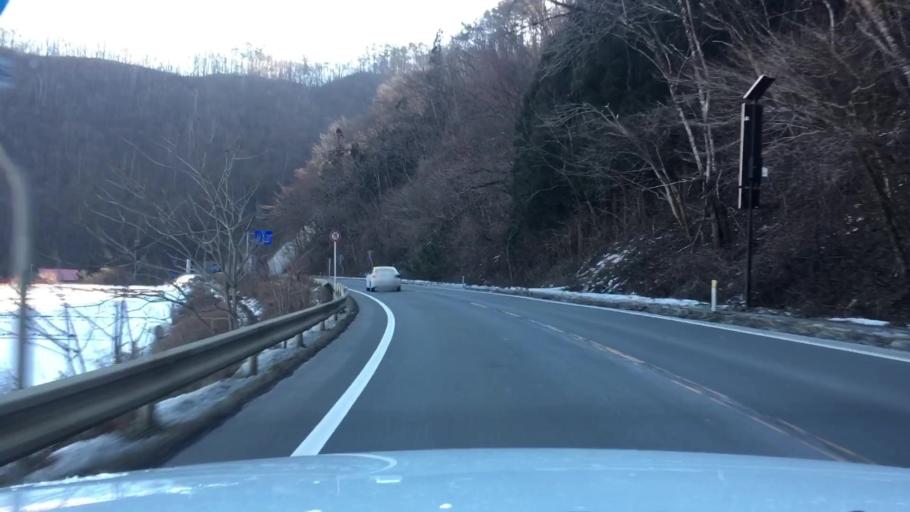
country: JP
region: Iwate
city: Tono
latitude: 39.6232
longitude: 141.6120
